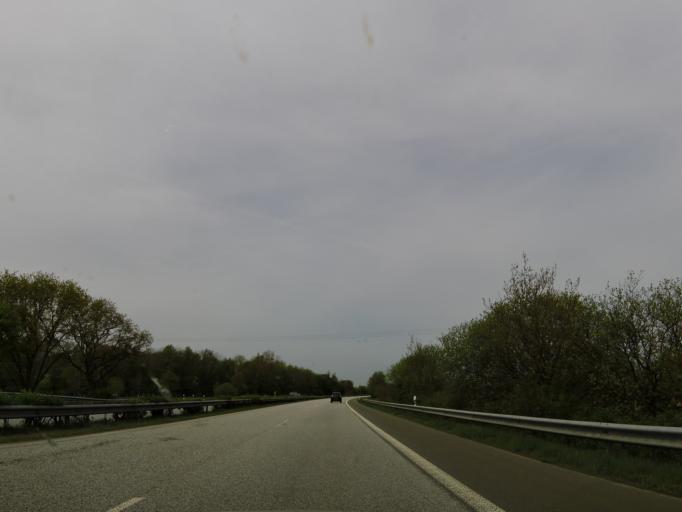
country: DE
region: Schleswig-Holstein
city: Schafstedt
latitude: 54.0745
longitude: 9.2869
